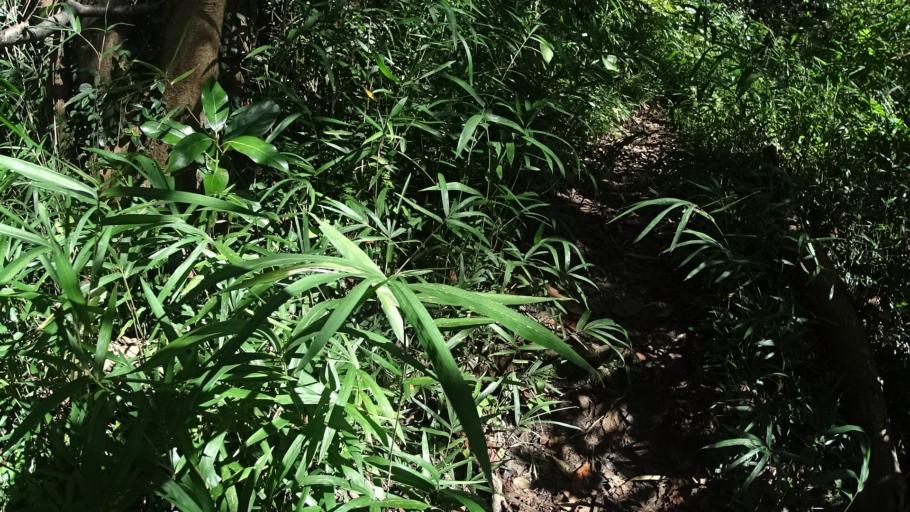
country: JP
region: Kanagawa
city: Hayama
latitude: 35.2738
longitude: 139.5941
